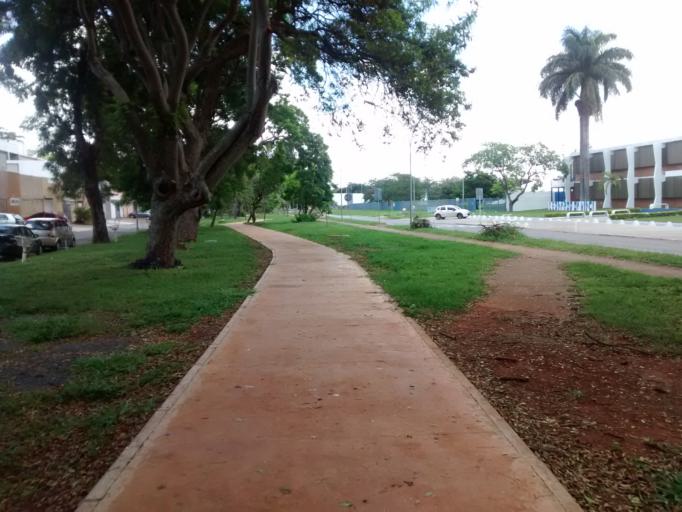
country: BR
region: Federal District
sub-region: Brasilia
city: Brasilia
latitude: -15.8003
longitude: -47.8969
